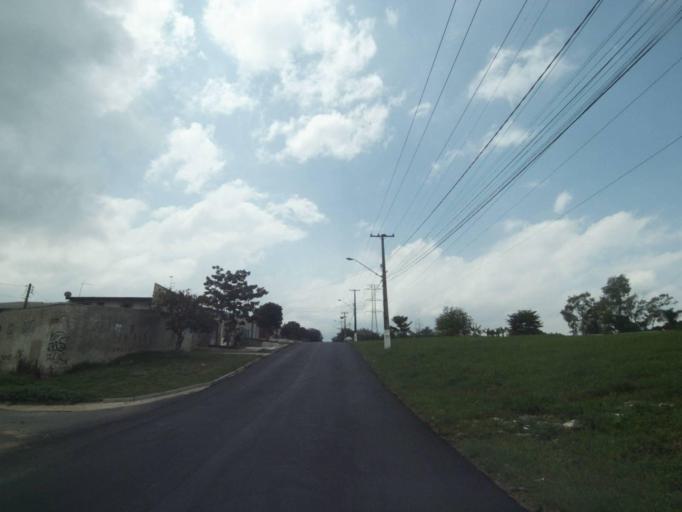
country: BR
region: Parana
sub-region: Curitiba
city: Curitiba
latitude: -25.4896
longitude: -49.3459
